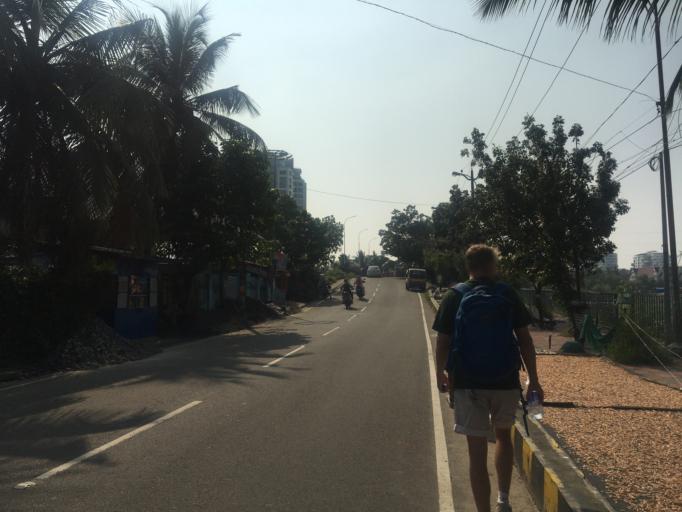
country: IN
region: Kerala
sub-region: Ernakulam
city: Cochin
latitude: 9.9546
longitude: 76.3145
